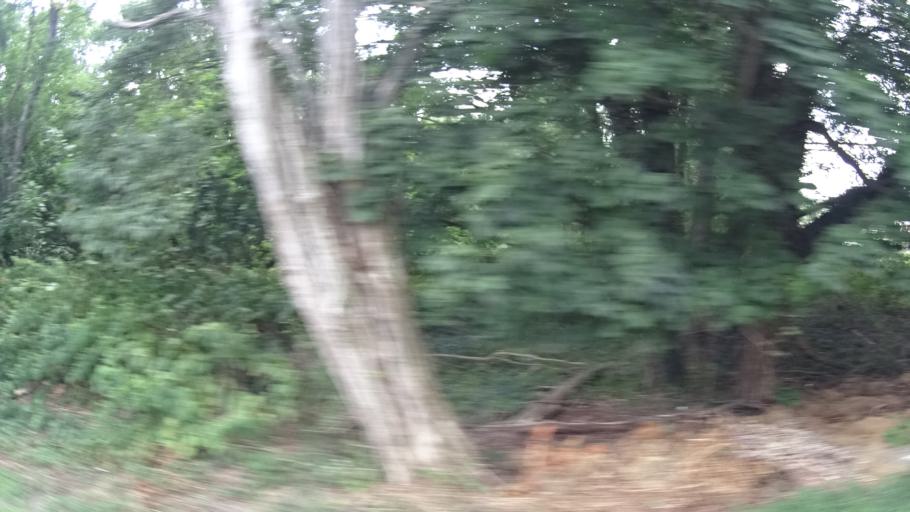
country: US
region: New Jersey
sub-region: Monmouth County
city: Manasquan
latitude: 40.1336
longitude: -74.0923
